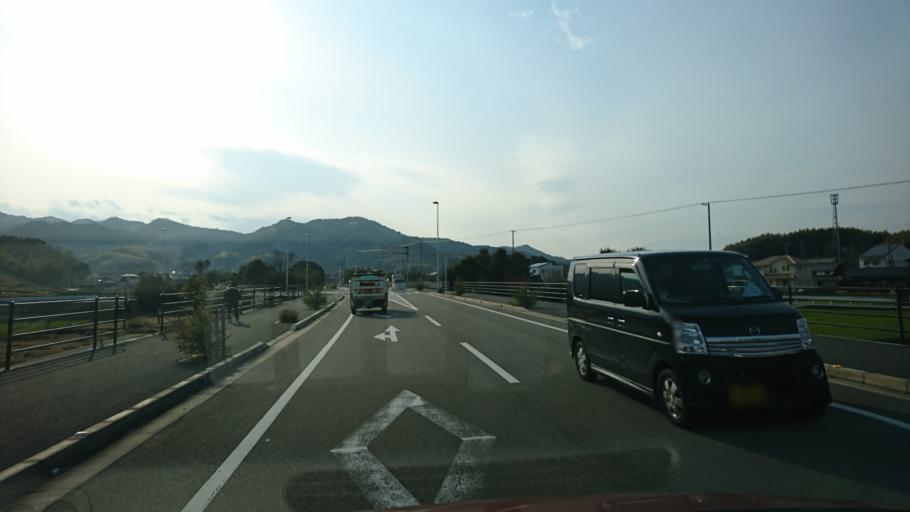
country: JP
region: Ehime
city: Saijo
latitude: 34.0232
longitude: 132.9969
